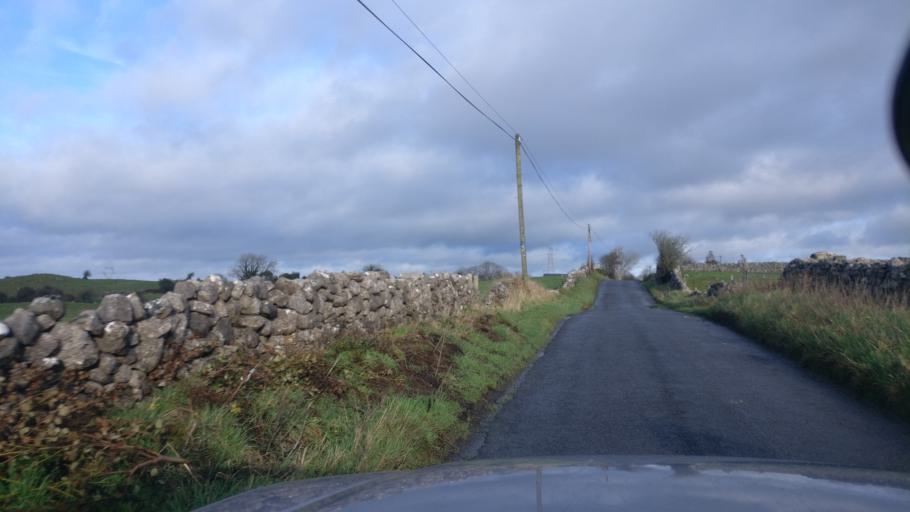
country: IE
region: Connaught
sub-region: County Galway
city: Loughrea
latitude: 53.2134
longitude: -8.5468
